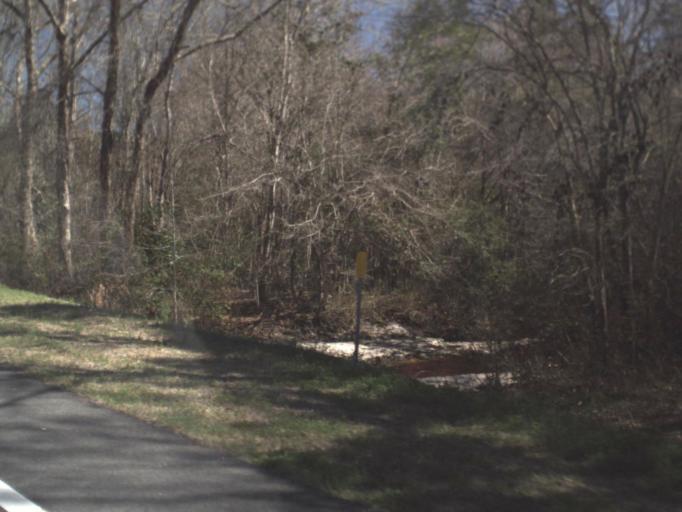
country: US
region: Florida
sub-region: Gadsden County
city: Quincy
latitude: 30.3956
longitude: -84.6785
